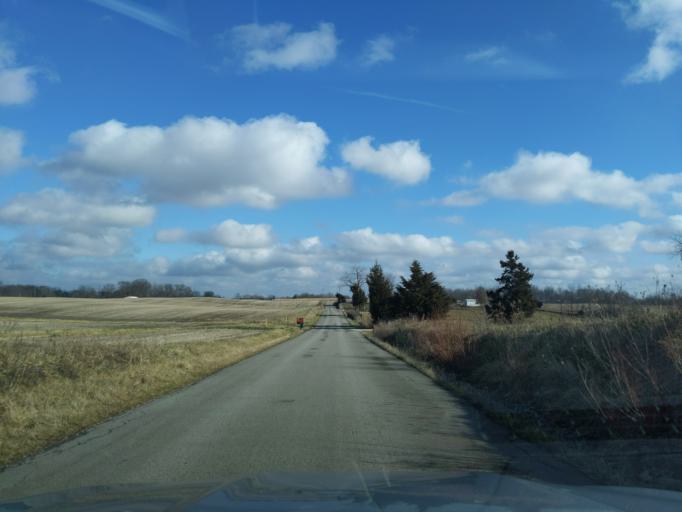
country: US
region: Indiana
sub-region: Decatur County
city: Greensburg
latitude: 39.2779
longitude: -85.4525
